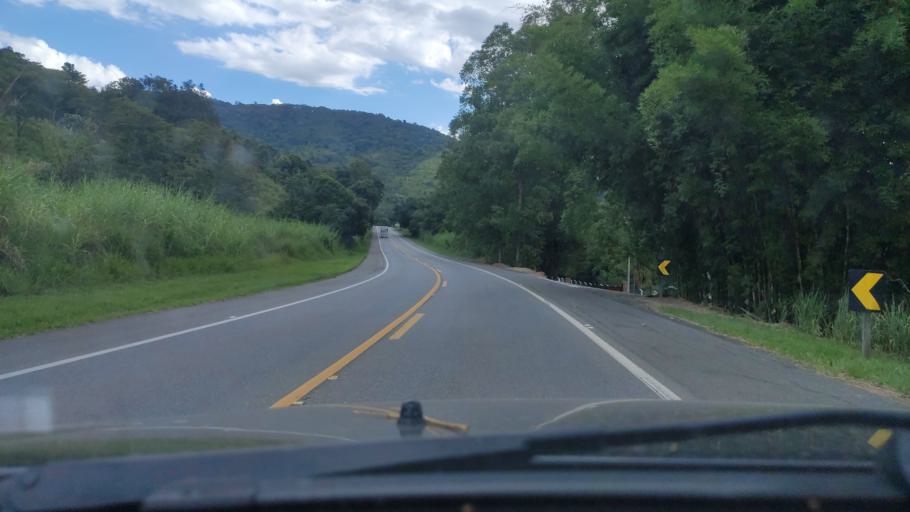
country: BR
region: Sao Paulo
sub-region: Aguas De Lindoia
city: Aguas de Lindoia
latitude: -22.4689
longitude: -46.7050
